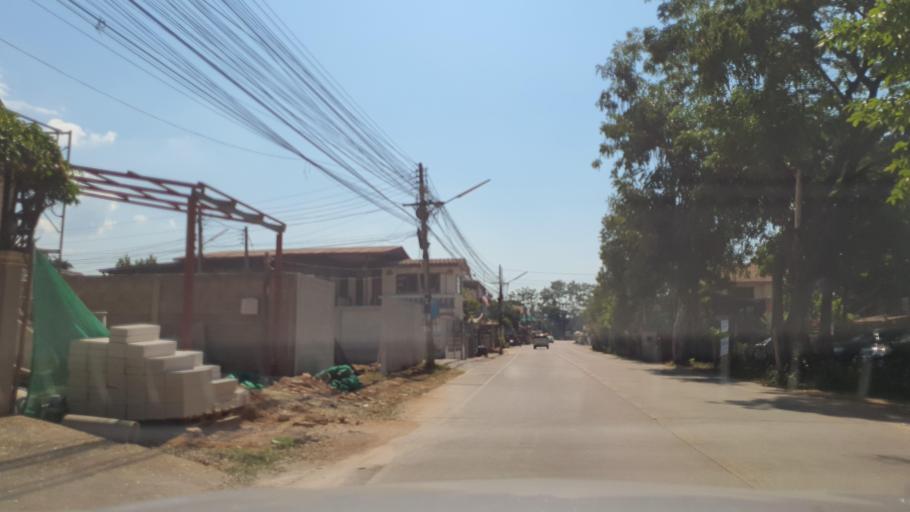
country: TH
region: Nan
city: Nan
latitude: 18.7725
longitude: 100.7678
